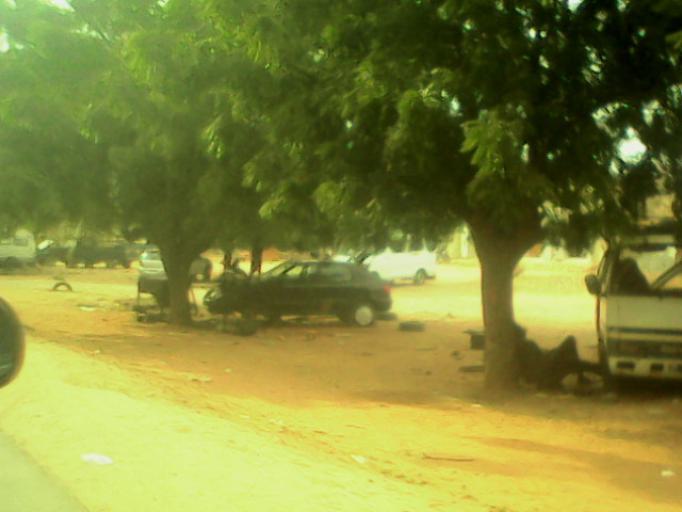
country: SN
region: Diourbel
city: Touba
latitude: 14.8844
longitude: -15.8786
